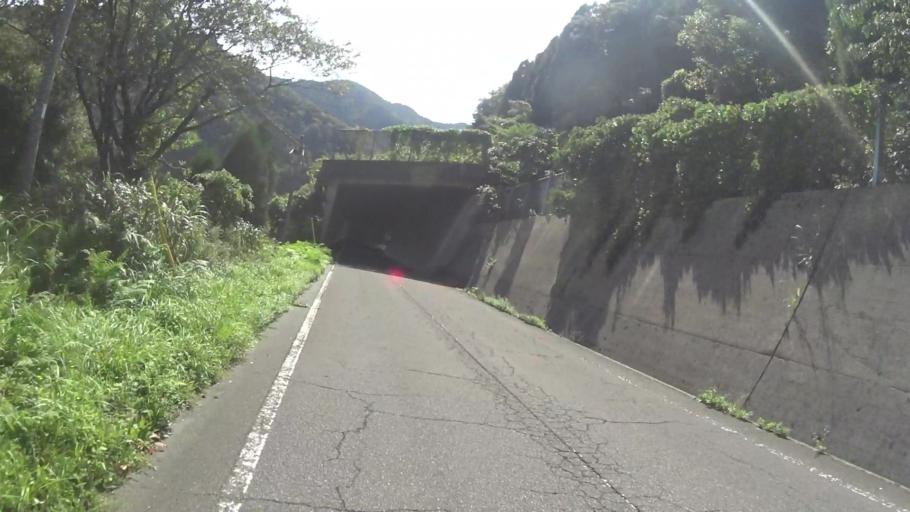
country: JP
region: Kyoto
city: Miyazu
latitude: 35.7031
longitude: 135.1872
